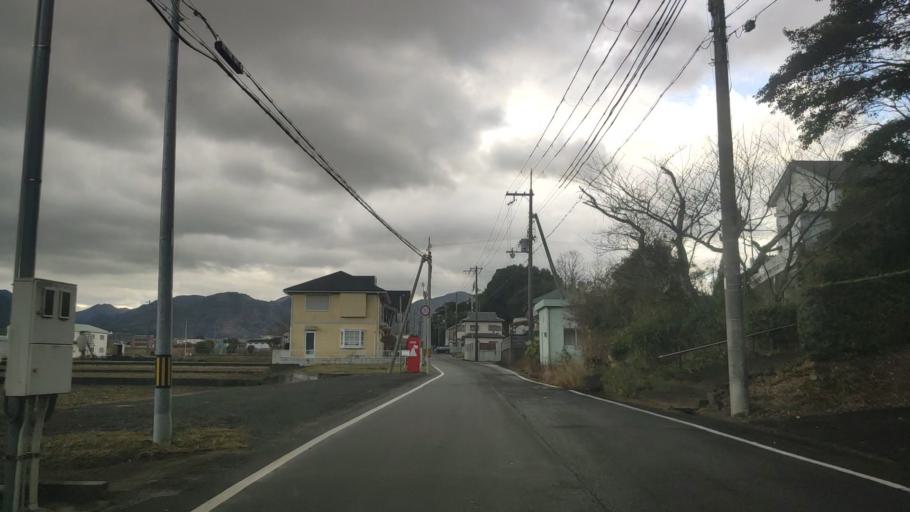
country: JP
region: Hyogo
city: Sumoto
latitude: 34.3310
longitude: 134.8533
